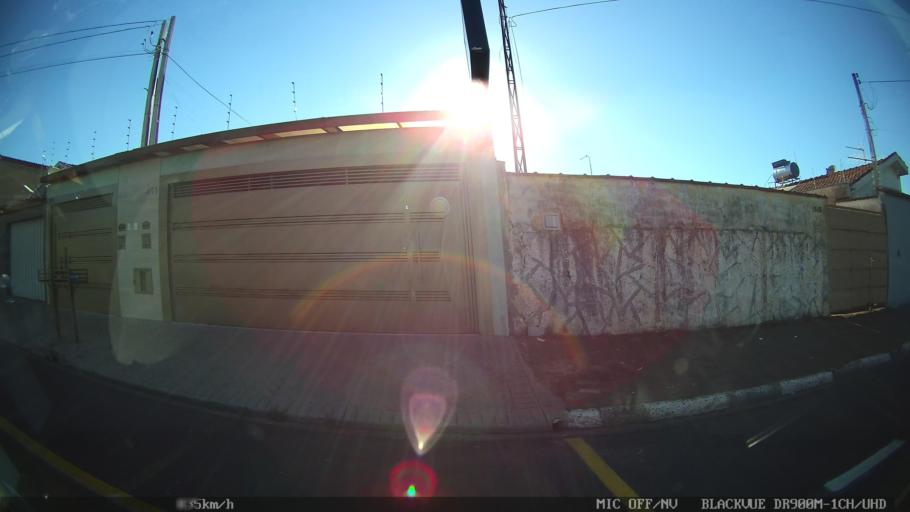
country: BR
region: Sao Paulo
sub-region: Franca
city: Franca
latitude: -20.5655
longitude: -47.3970
